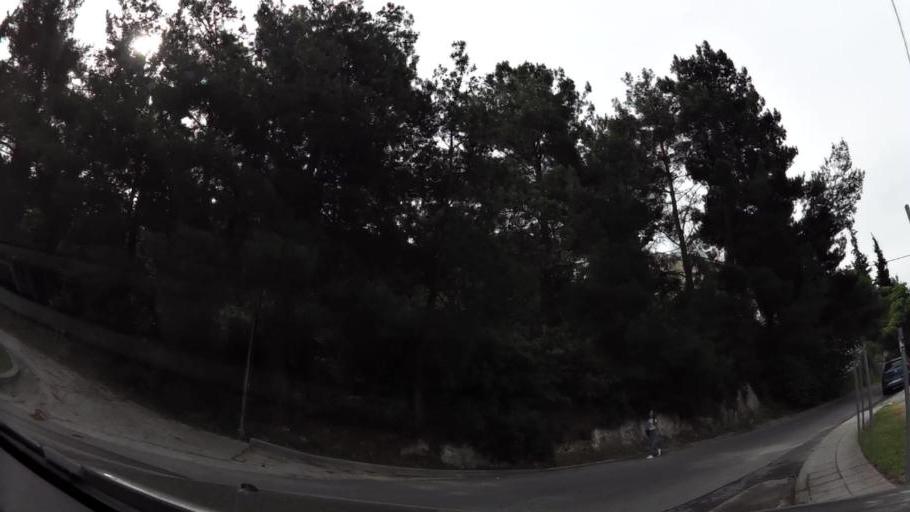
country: GR
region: Central Macedonia
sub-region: Nomos Thessalonikis
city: Panorama
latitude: 40.5914
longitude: 23.0277
